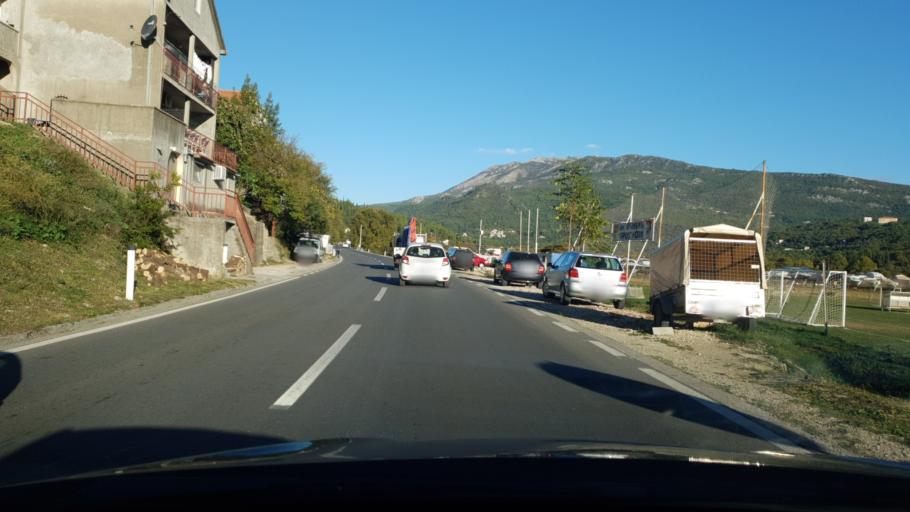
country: ME
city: Igalo
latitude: 42.4584
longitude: 18.4909
